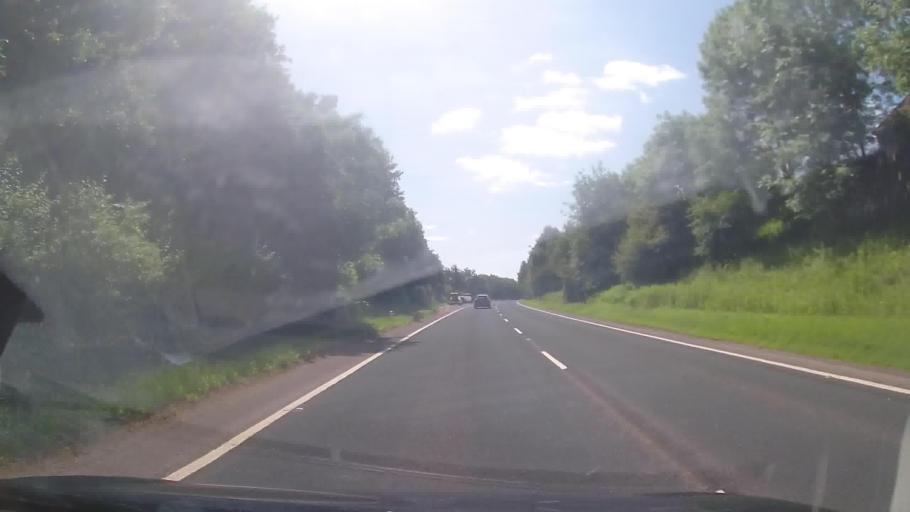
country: GB
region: England
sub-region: Shropshire
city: Ludlow
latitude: 52.3740
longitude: -2.6993
